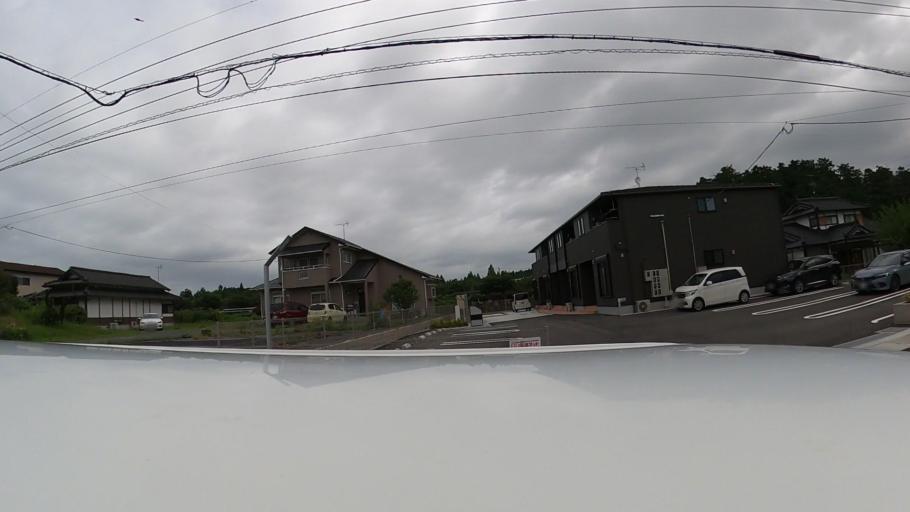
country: JP
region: Kumamoto
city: Ozu
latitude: 32.8368
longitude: 130.8790
